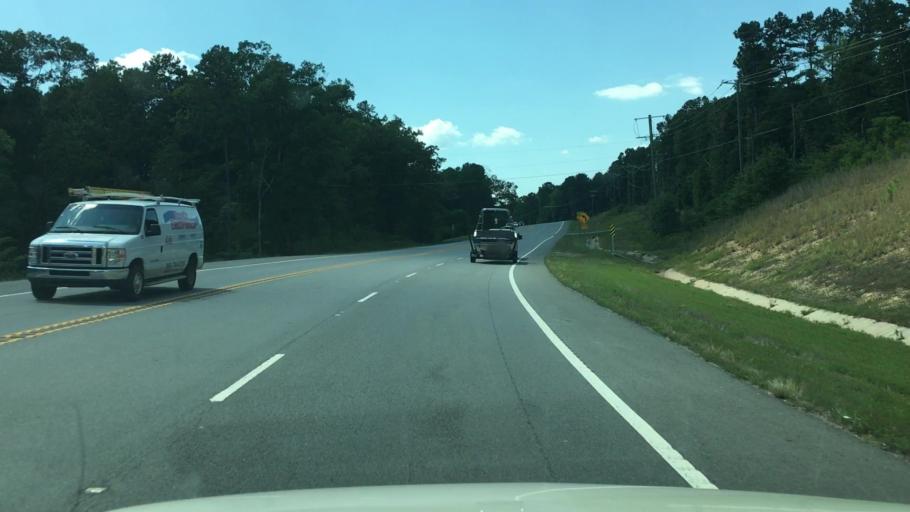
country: US
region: Arkansas
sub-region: Garland County
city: Piney
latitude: 34.5080
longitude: -93.1900
